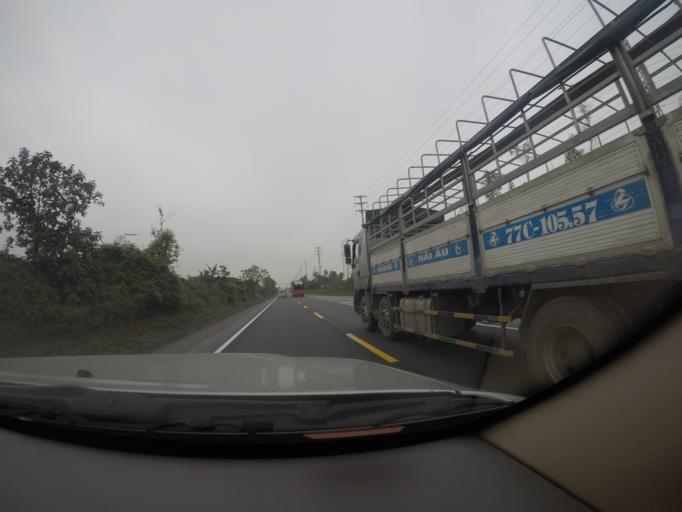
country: VN
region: Ha Tinh
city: Ky Anh
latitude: 18.0265
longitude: 106.3508
